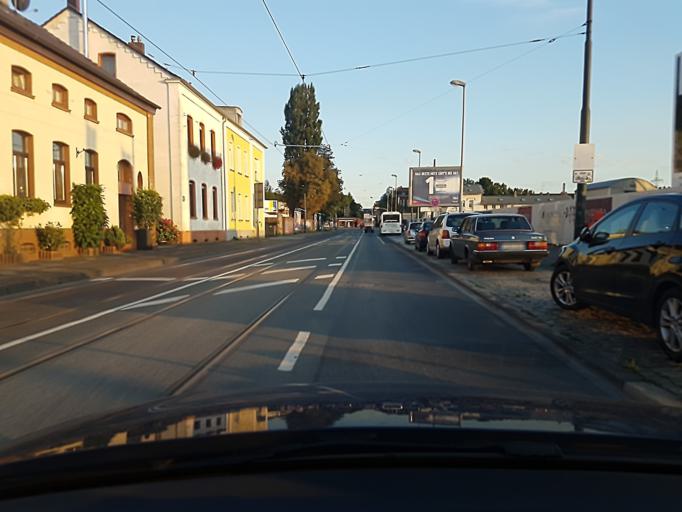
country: DE
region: North Rhine-Westphalia
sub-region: Regierungsbezirk Dusseldorf
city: Erkrath
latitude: 51.2221
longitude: 6.8654
